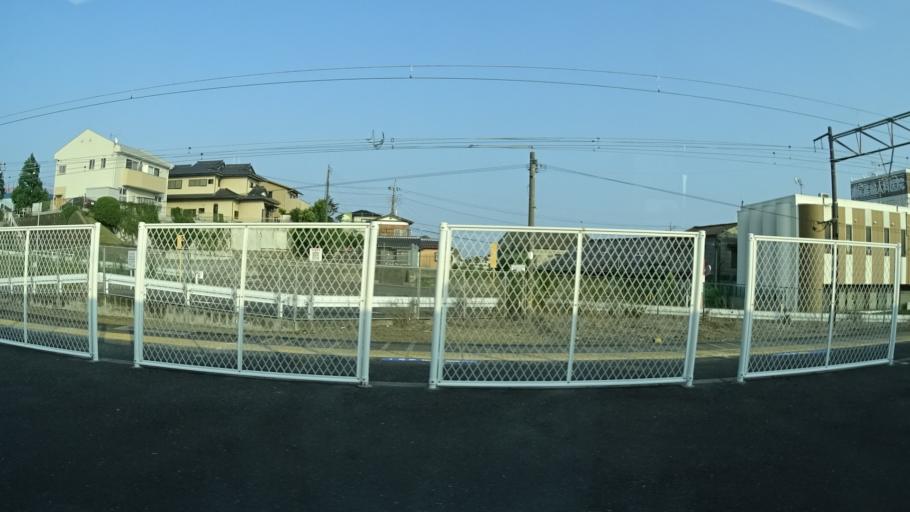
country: JP
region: Ibaraki
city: Hitachi
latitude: 36.5514
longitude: 140.6316
